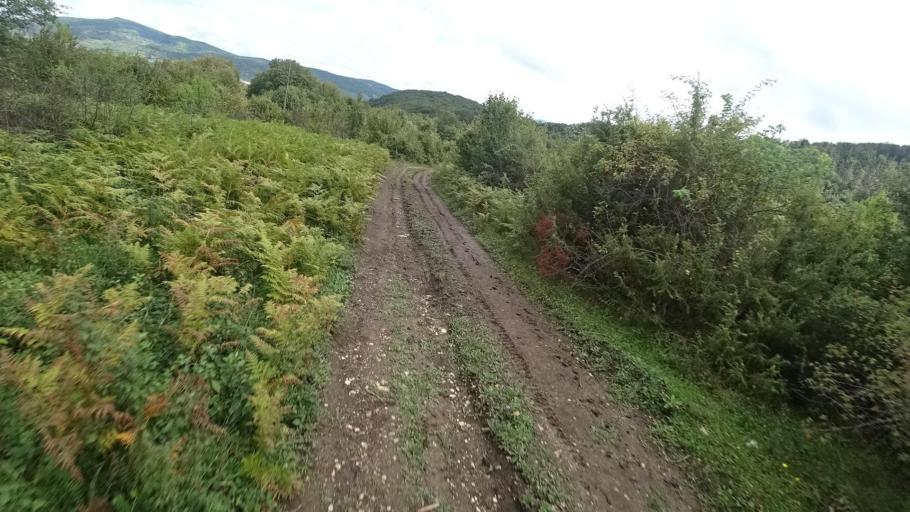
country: BA
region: Republika Srpska
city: Bronzani Majdan
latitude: 44.6460
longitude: 17.0139
